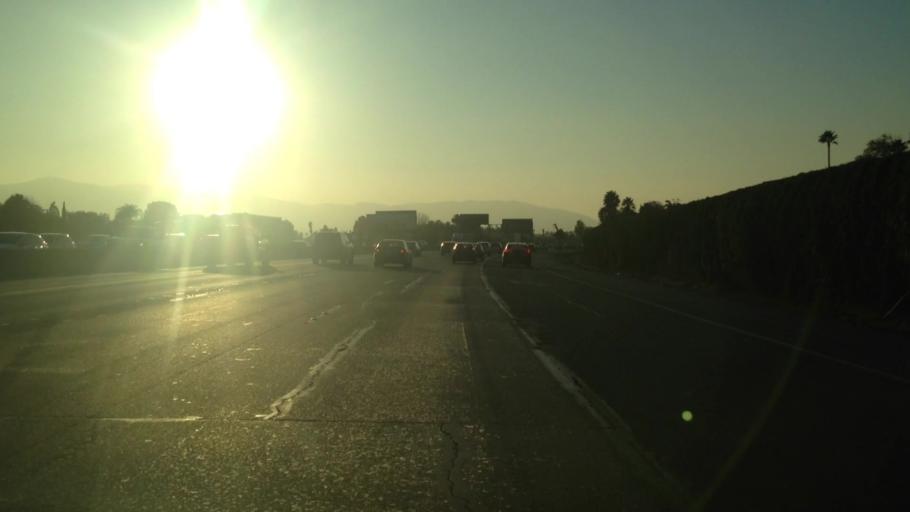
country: US
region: California
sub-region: Riverside County
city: Home Gardens
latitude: 33.8977
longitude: -117.4788
